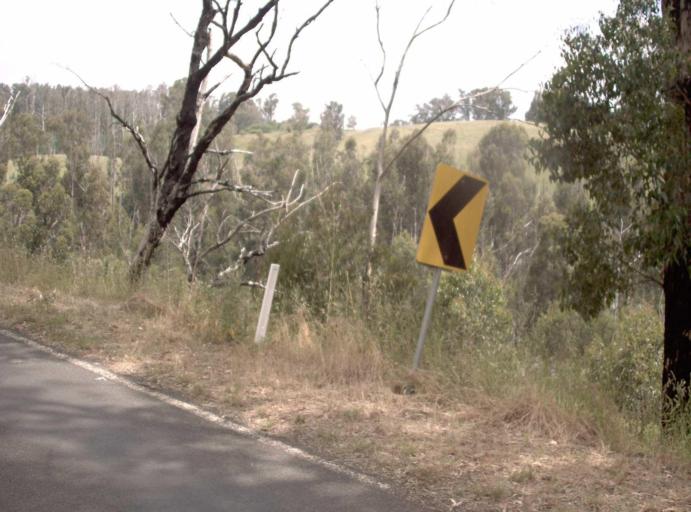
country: AU
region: Victoria
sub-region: Latrobe
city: Traralgon
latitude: -38.3251
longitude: 146.5712
